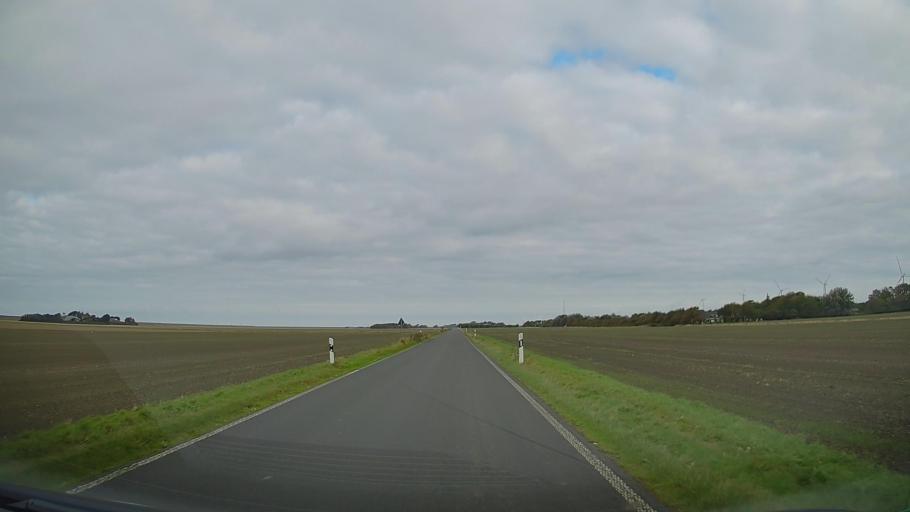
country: DE
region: Schleswig-Holstein
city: Friedrich-Wilhelm-Lubke-Koog
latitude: 54.8574
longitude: 8.6242
